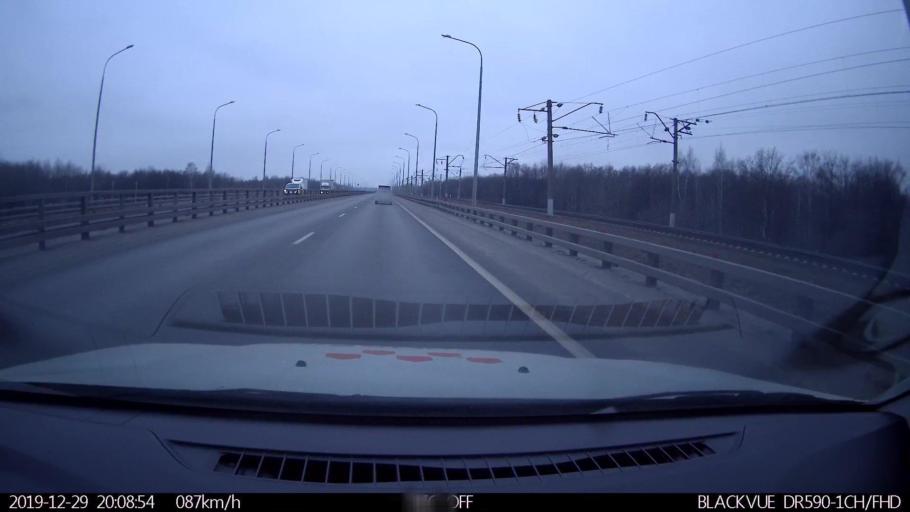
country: RU
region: Nizjnij Novgorod
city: Neklyudovo
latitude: 56.3803
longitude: 43.9596
